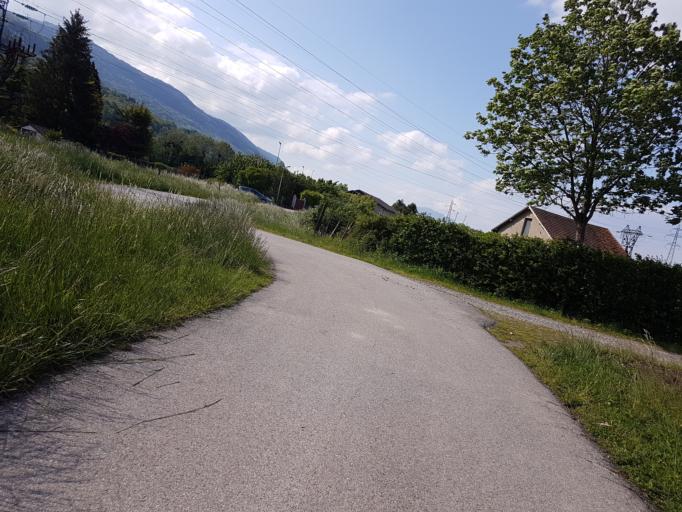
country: FR
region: Rhone-Alpes
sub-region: Departement de la Savoie
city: Chindrieux
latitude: 45.8871
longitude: 5.8403
